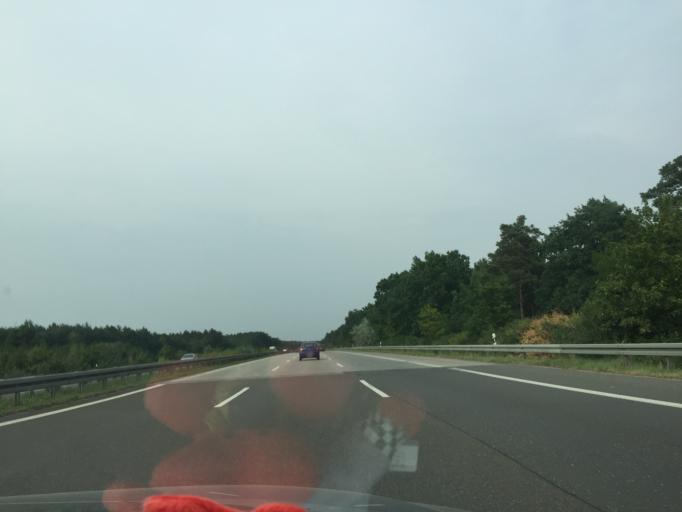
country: DE
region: Brandenburg
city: Erkner
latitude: 52.3502
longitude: 13.7574
